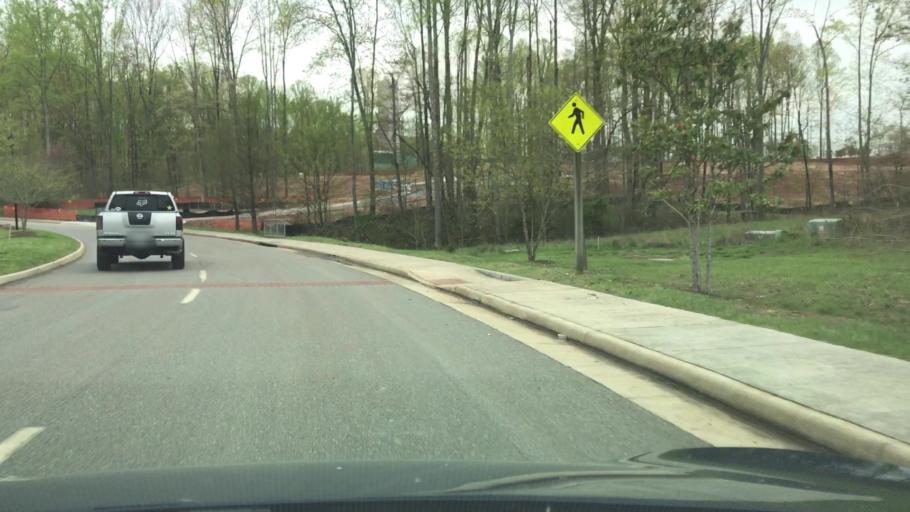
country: US
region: Virginia
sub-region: Bedford County
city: Forest
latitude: 37.3040
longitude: -79.3379
